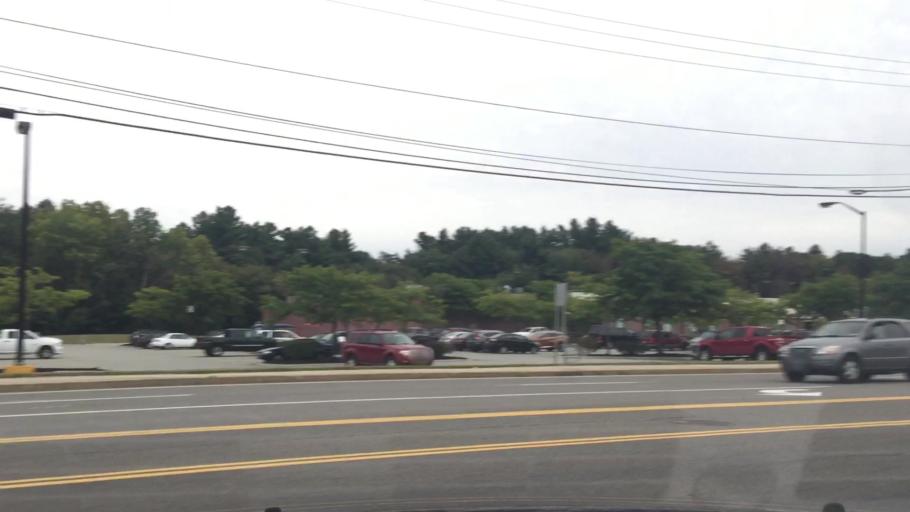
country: US
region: New Hampshire
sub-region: Hillsborough County
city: Hudson
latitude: 42.7335
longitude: -71.4257
